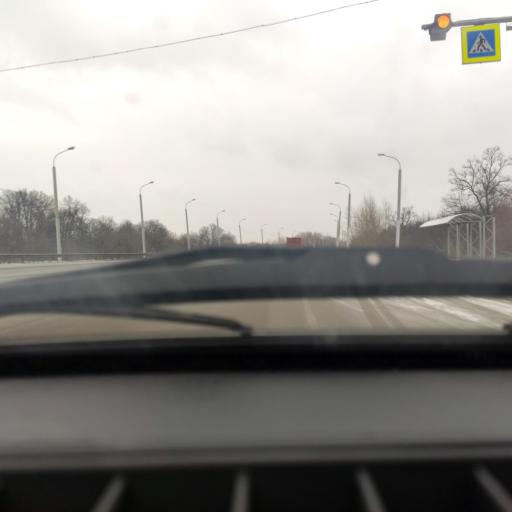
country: RU
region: Bashkortostan
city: Iglino
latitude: 54.7983
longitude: 56.2030
